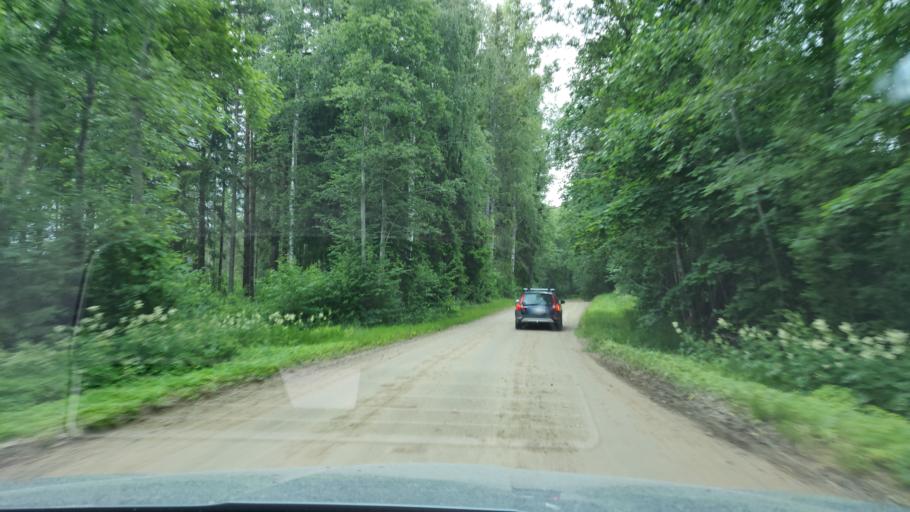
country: EE
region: Vorumaa
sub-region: Antsla vald
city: Vana-Antsla
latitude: 58.0329
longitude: 26.5516
